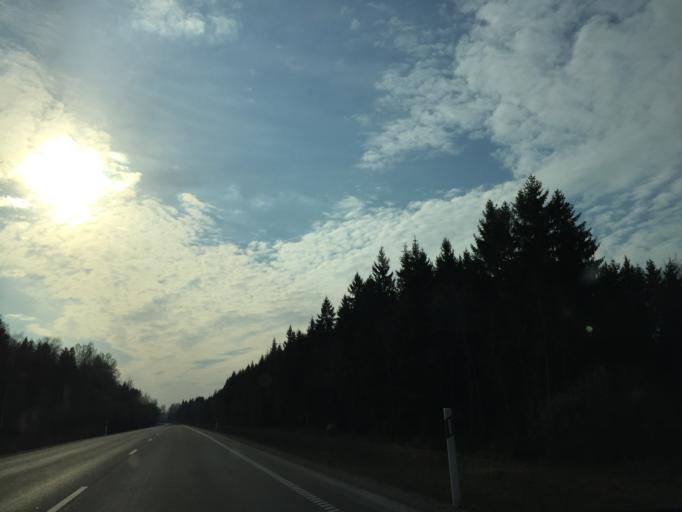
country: EE
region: Jogevamaa
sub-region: Mustvee linn
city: Mustvee
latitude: 58.8471
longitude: 26.8993
